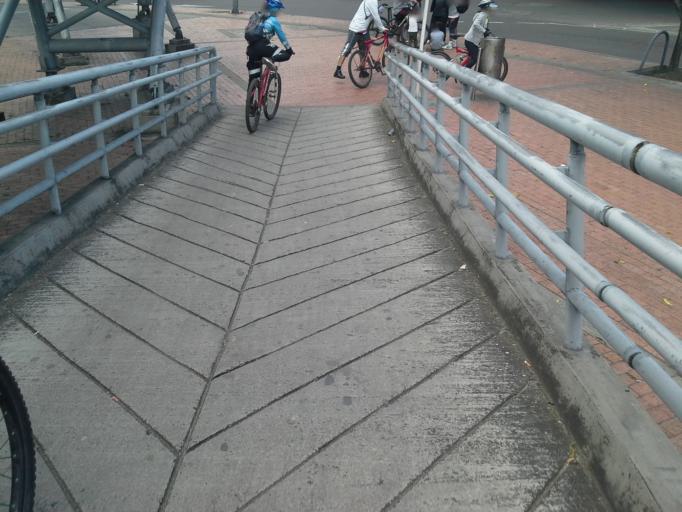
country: CO
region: Bogota D.C.
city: Bogota
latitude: 4.5933
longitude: -74.1262
